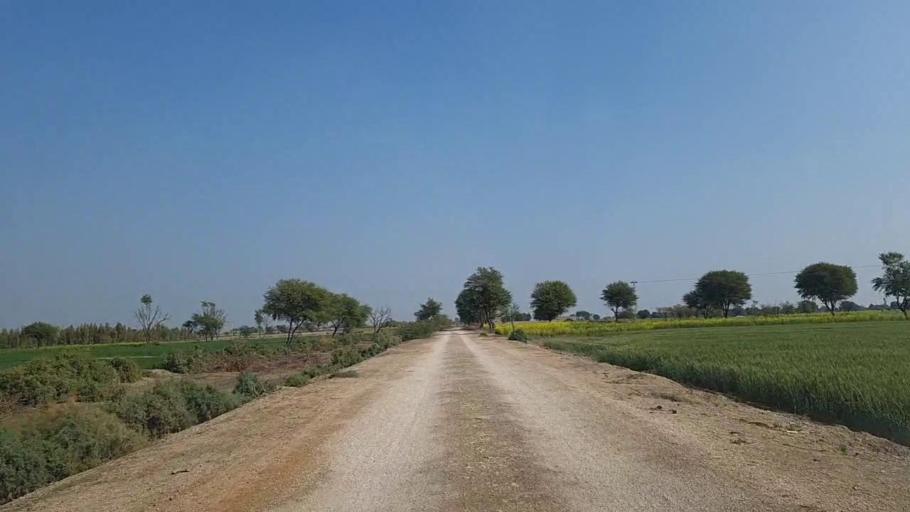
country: PK
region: Sindh
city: Jam Sahib
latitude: 26.2540
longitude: 68.5681
